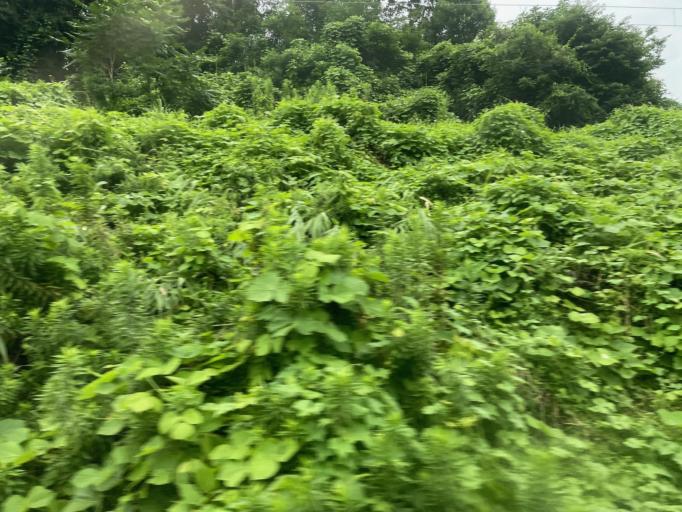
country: JP
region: Fukushima
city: Motomiya
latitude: 37.5527
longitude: 140.4066
